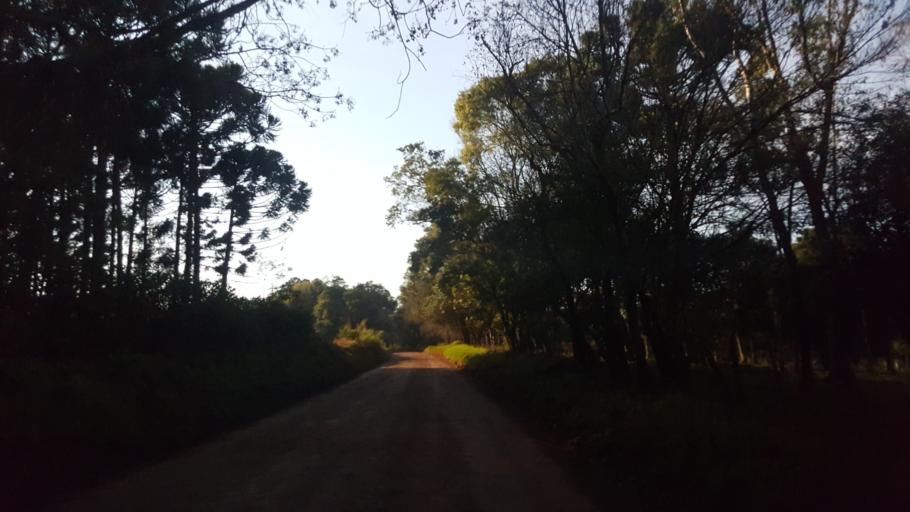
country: AR
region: Misiones
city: Capiovi
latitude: -26.8920
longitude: -55.0612
